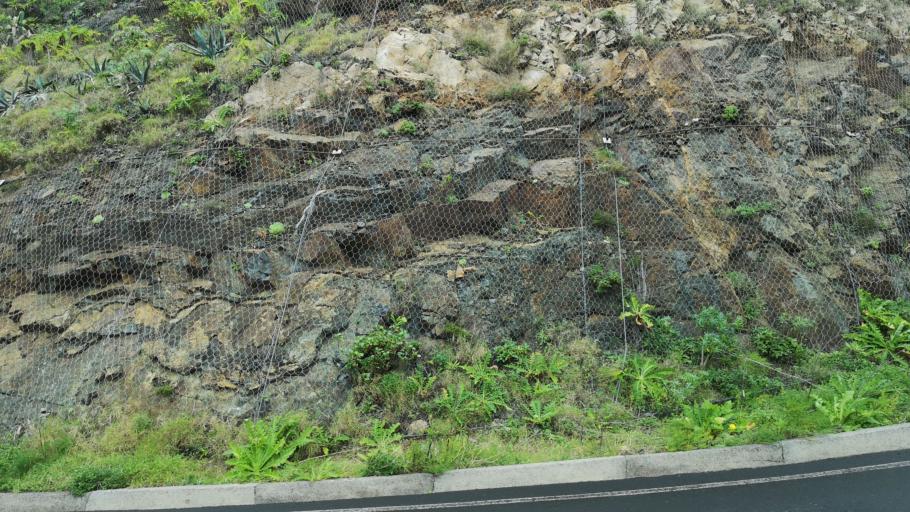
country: ES
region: Canary Islands
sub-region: Provincia de Santa Cruz de Tenerife
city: Agulo
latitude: 28.1882
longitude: -17.2158
